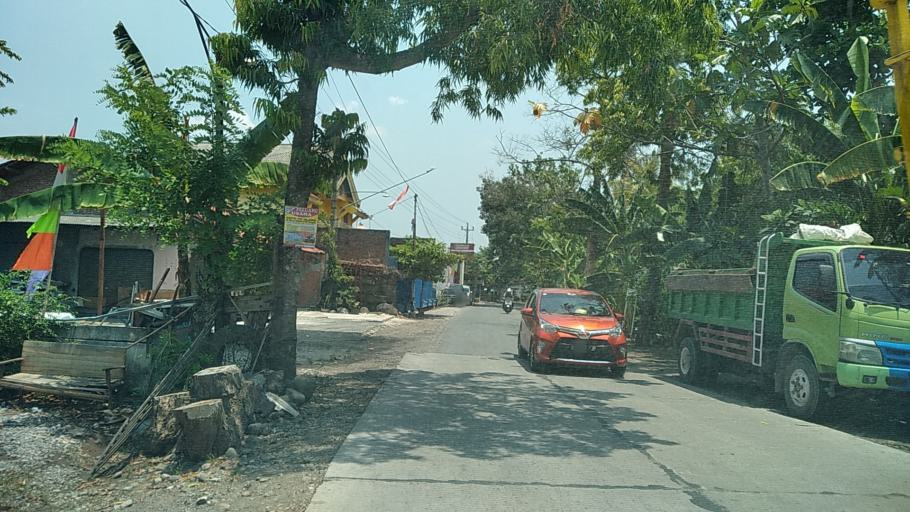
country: ID
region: Central Java
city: Mranggen
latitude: -7.0112
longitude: 110.4874
